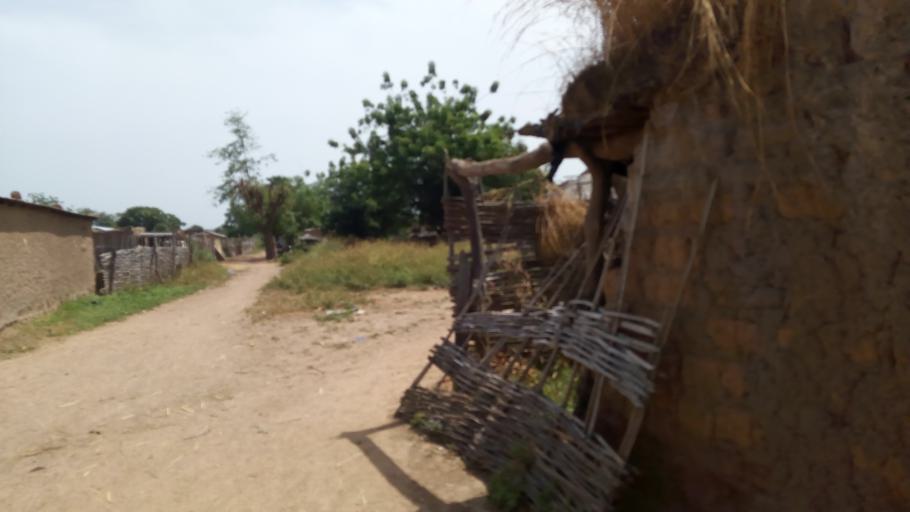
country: ML
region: Kayes
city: Kita
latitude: 13.3996
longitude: -8.8599
